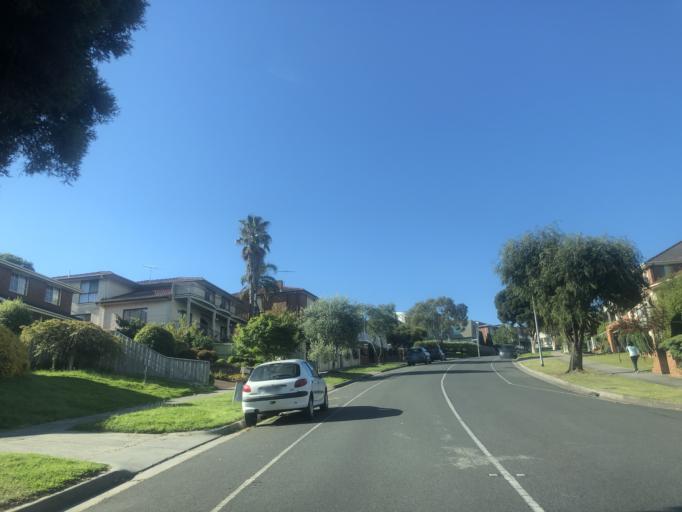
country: AU
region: Victoria
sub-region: Monash
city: Mulgrave
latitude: -37.9188
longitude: 145.1930
